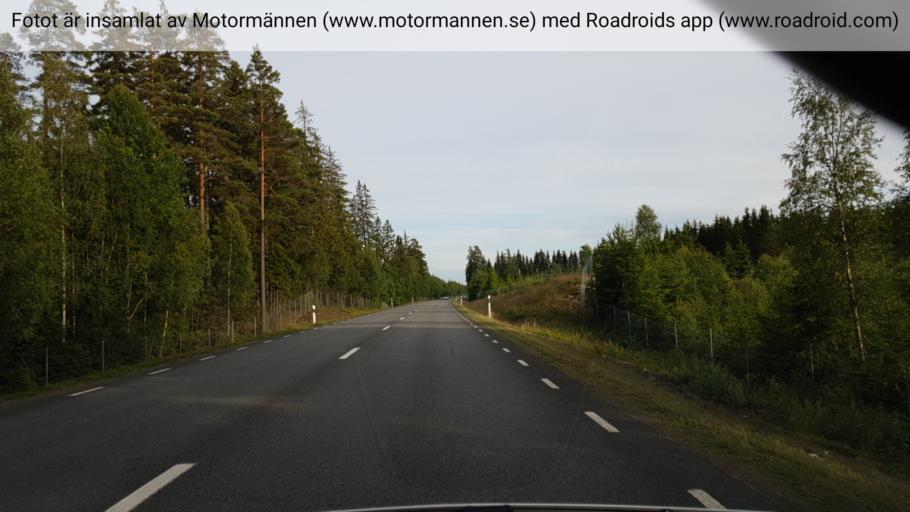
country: SE
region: Vaestra Goetaland
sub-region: Skara Kommun
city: Skara
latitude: 58.3530
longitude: 13.4291
